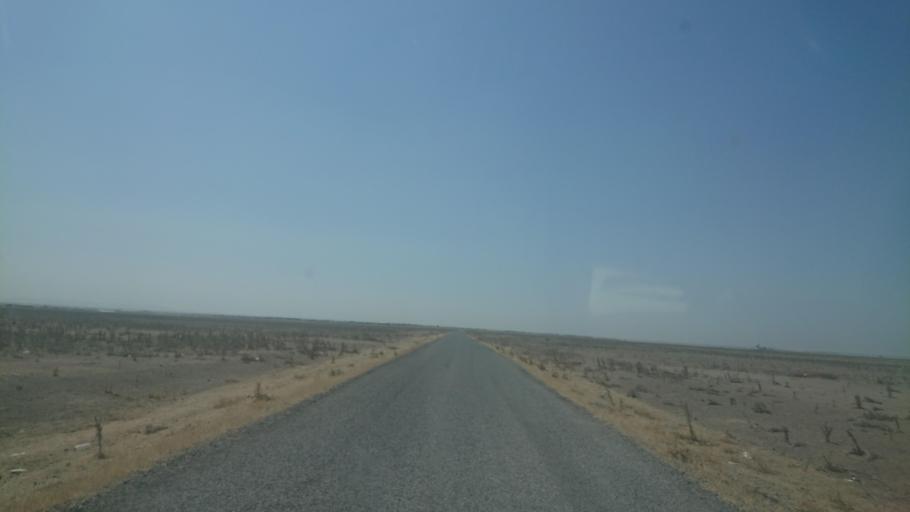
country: TR
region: Aksaray
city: Yesilova
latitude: 38.3213
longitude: 33.7437
